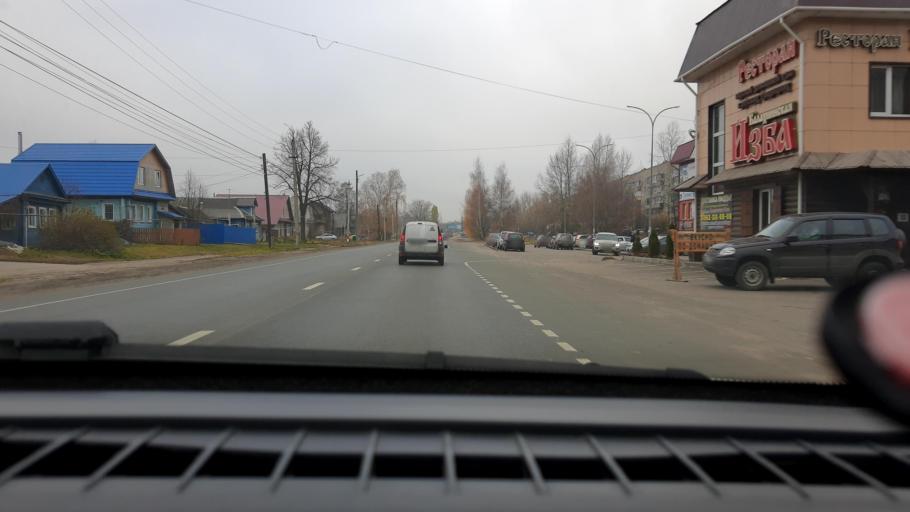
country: RU
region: Nizjnij Novgorod
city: Novaya Balakhna
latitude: 56.5177
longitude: 43.5796
